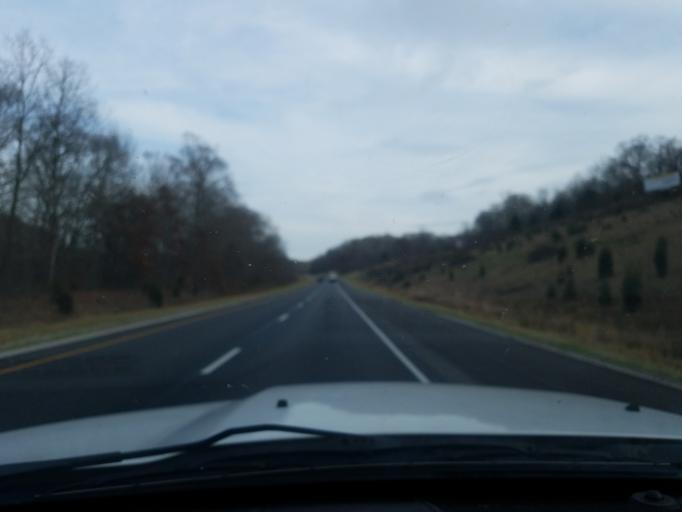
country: US
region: Indiana
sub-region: Crawford County
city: English
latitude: 38.2358
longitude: -86.3799
